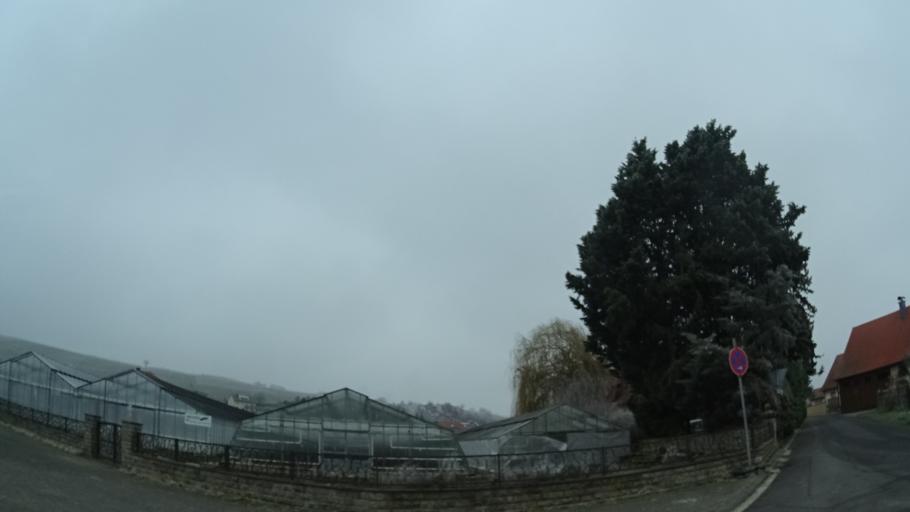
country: DE
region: Bavaria
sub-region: Regierungsbezirk Unterfranken
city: Segnitz
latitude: 49.6726
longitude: 10.1409
